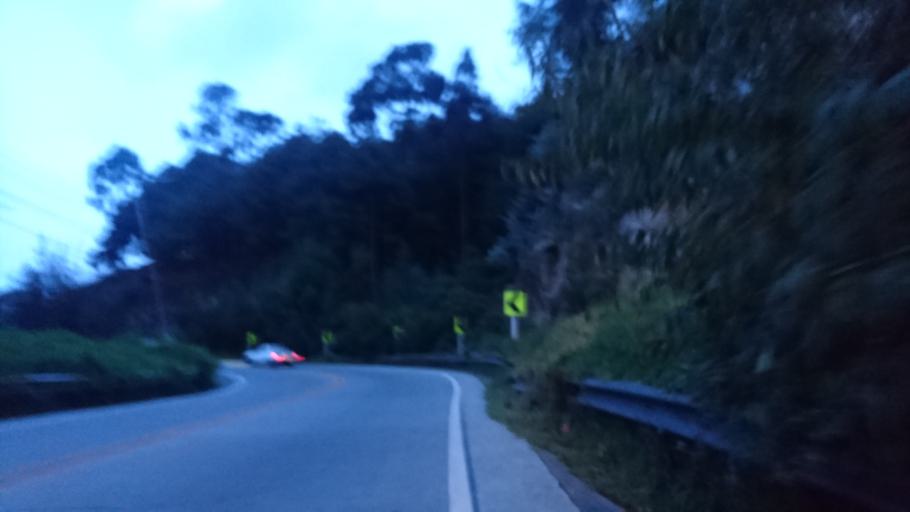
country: CO
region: Bogota D.C.
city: Barrio San Luis
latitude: 4.6718
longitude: -74.0387
